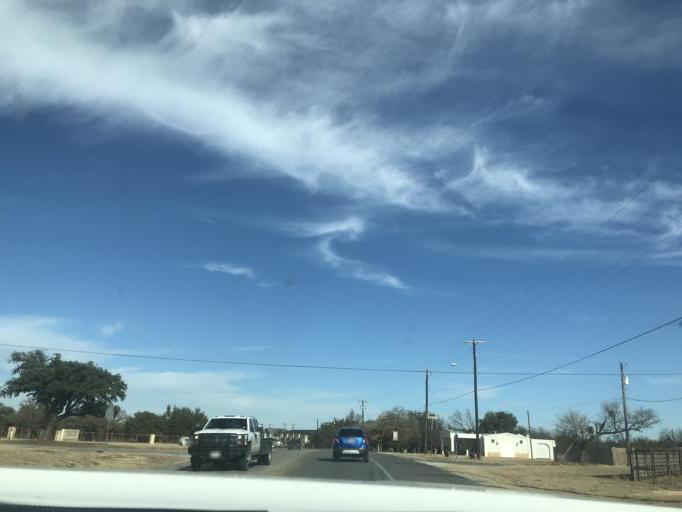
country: US
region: Texas
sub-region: Erath County
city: Stephenville
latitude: 32.2359
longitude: -98.2020
